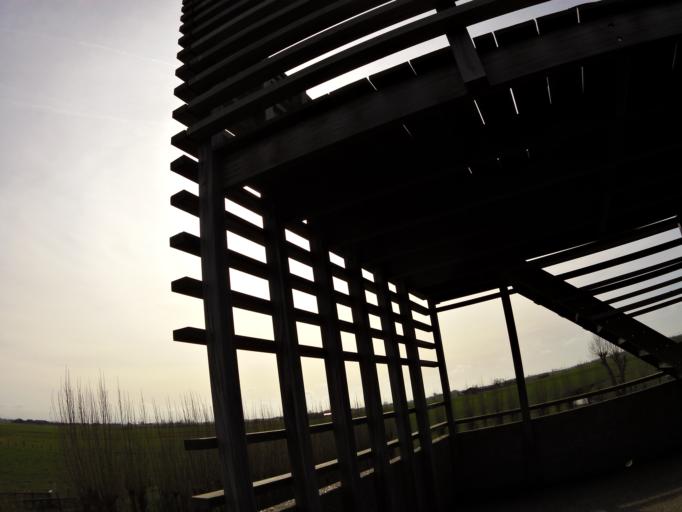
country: BE
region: Flanders
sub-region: Provincie West-Vlaanderen
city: Diksmuide
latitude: 51.0587
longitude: 2.8323
